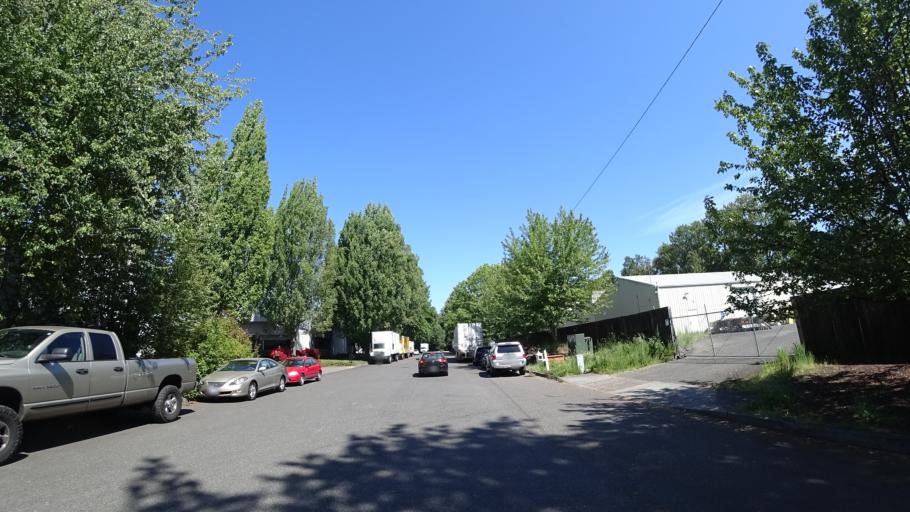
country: US
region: Oregon
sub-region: Multnomah County
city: Lents
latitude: 45.5674
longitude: -122.5646
